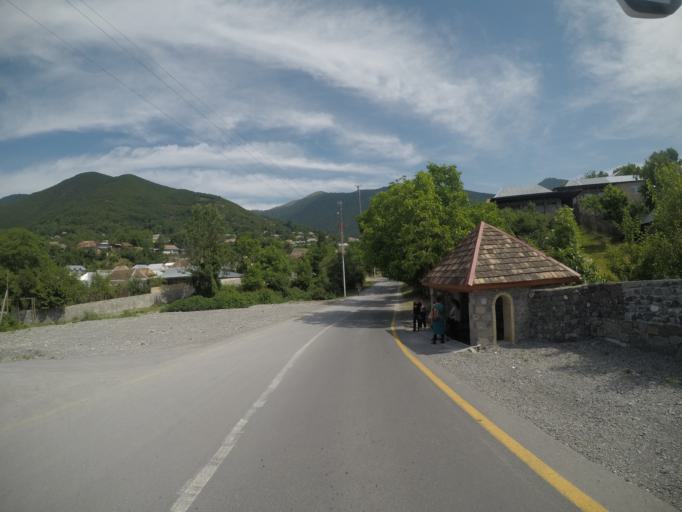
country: AZ
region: Shaki City
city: Sheki
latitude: 41.2464
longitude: 47.1886
